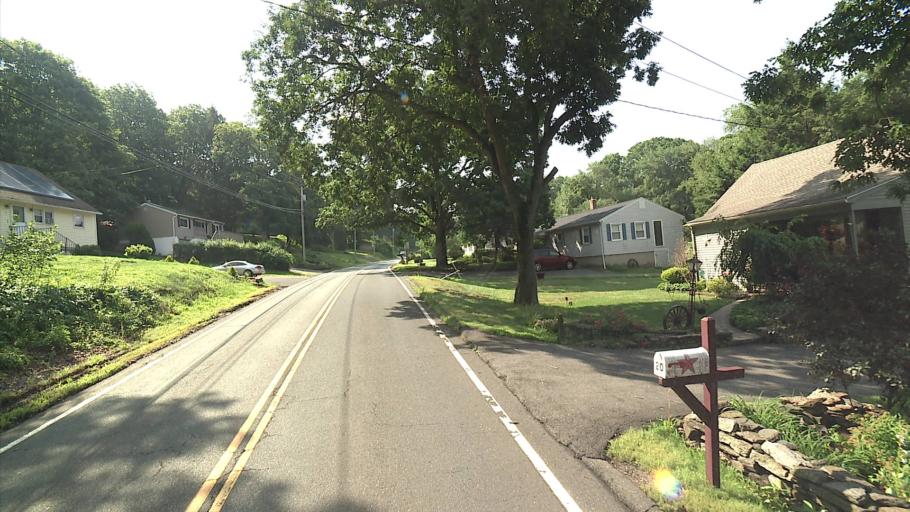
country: US
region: Connecticut
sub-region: New Haven County
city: Wolcott
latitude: 41.5955
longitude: -72.9595
